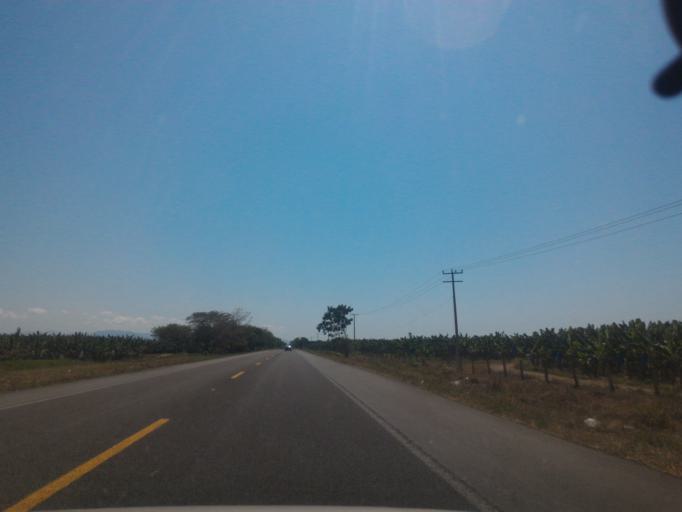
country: MX
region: Colima
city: Tecoman
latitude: 18.8113
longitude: -103.8036
